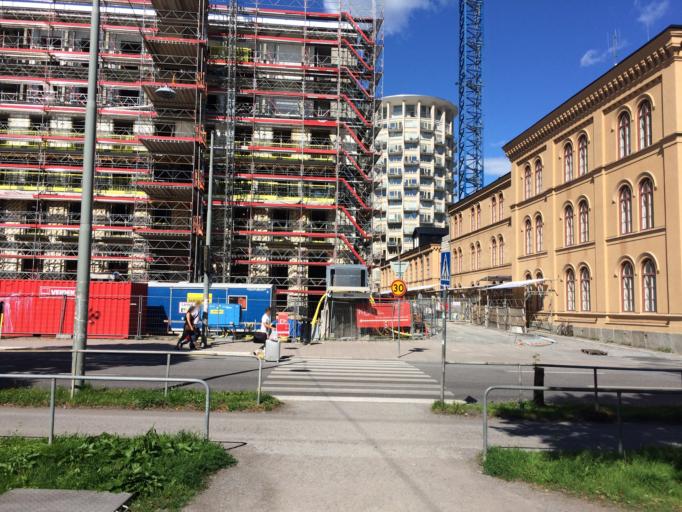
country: SE
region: Stockholm
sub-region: Stockholms Kommun
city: OEstermalm
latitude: 59.3430
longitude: 18.0819
